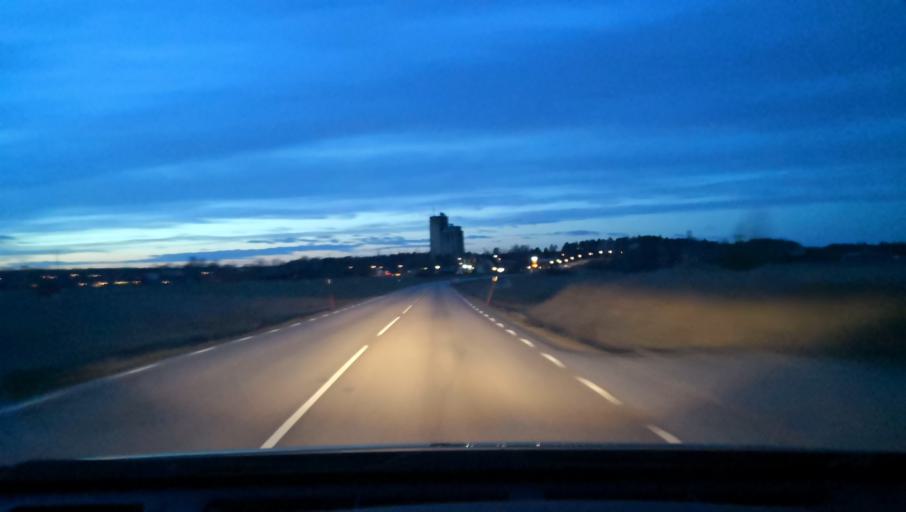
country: SE
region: Uppsala
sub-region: Enkopings Kommun
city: Grillby
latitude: 59.6185
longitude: 17.2638
